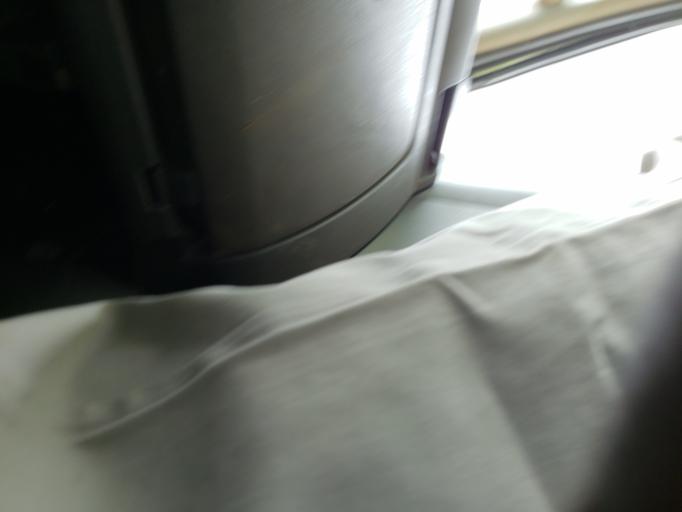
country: ML
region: Koulikoro
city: Kangaba
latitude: 12.0241
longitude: -8.7146
